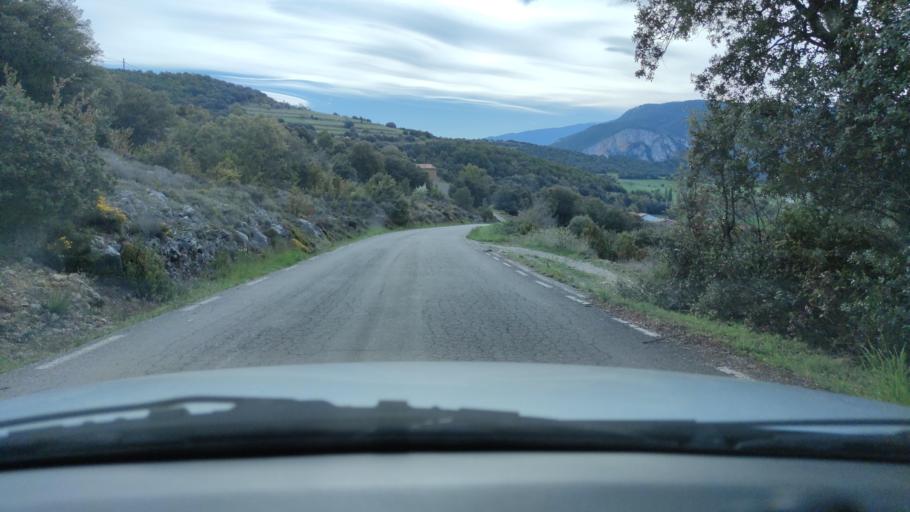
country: ES
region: Catalonia
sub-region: Provincia de Lleida
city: Coll de Nargo
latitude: 42.2374
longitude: 1.3829
